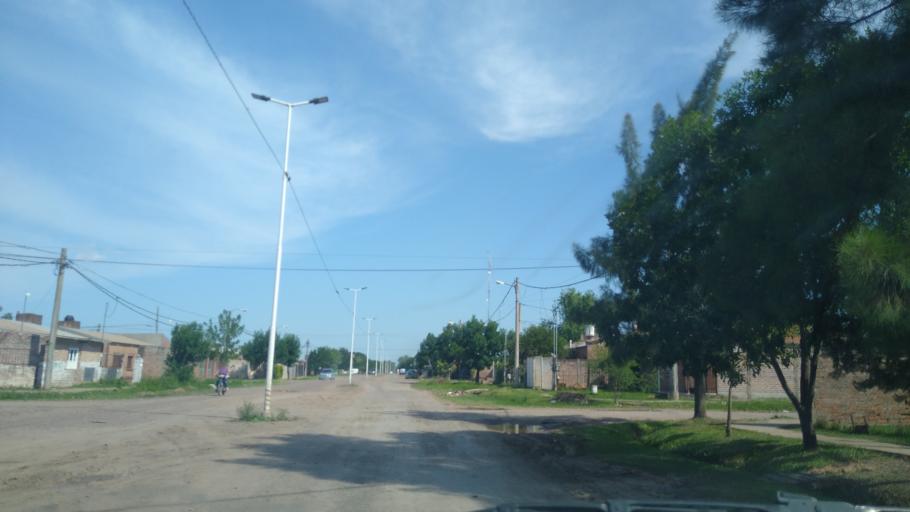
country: AR
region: Chaco
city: Puerto Vilelas
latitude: -27.4978
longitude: -58.9626
